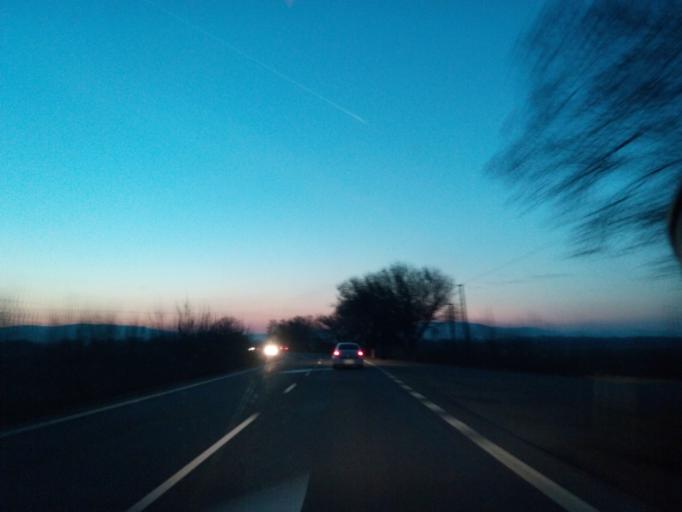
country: SK
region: Kosicky
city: Trebisov
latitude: 48.6995
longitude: 21.7901
